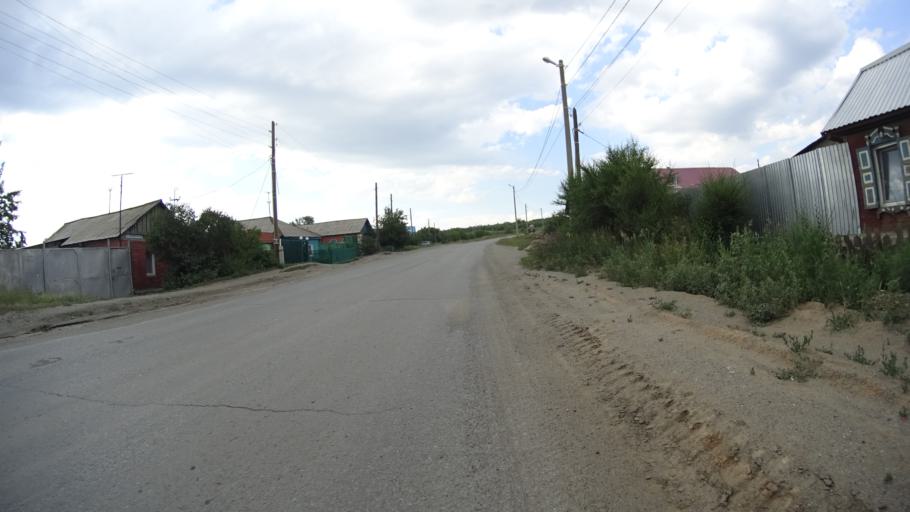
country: RU
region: Chelyabinsk
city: Troitsk
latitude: 54.0989
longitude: 61.5912
